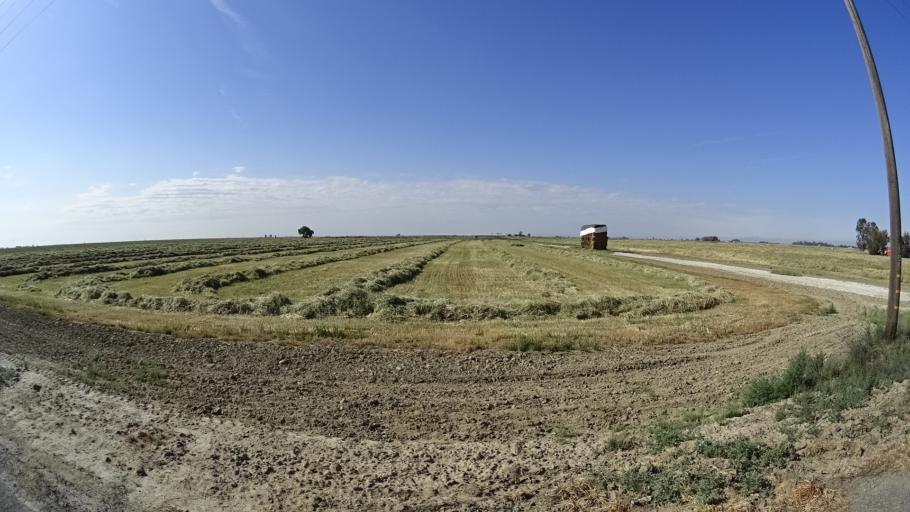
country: US
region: California
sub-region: Kings County
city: Stratford
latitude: 36.2257
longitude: -119.7599
